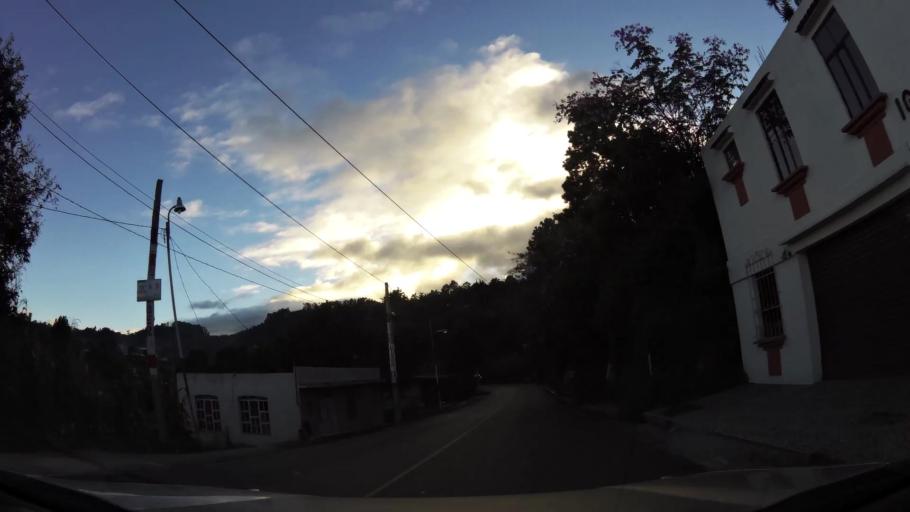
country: GT
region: Quiche
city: Chichicastenango
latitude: 14.9355
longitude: -91.1088
